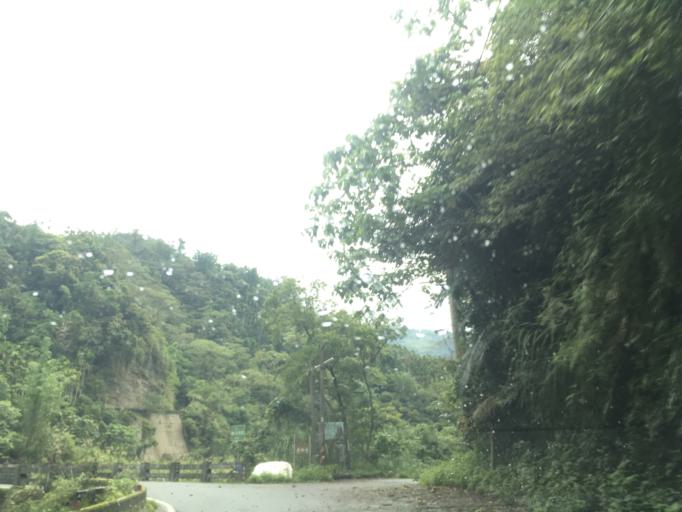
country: TW
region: Taiwan
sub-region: Yunlin
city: Douliu
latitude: 23.5647
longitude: 120.6404
